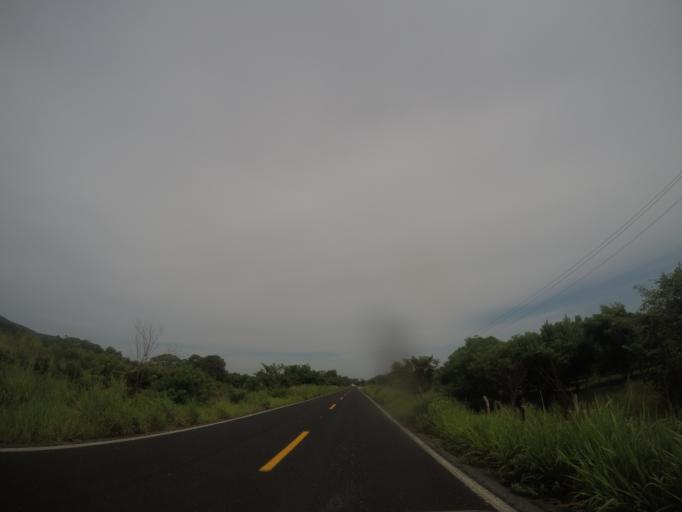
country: MX
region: Oaxaca
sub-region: Villa de Tututepec de Melchor Ocampo
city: Santa Rosa de Lima
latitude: 16.0263
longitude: -97.5620
